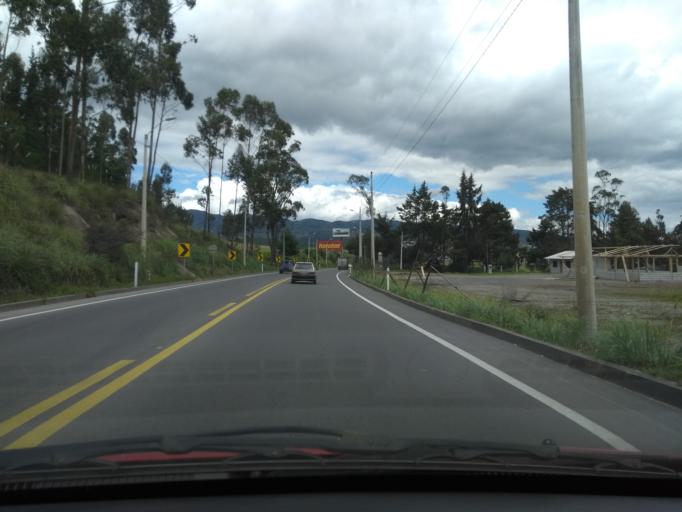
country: EC
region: Azuay
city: Cuenca
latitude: -3.0362
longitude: -79.0417
